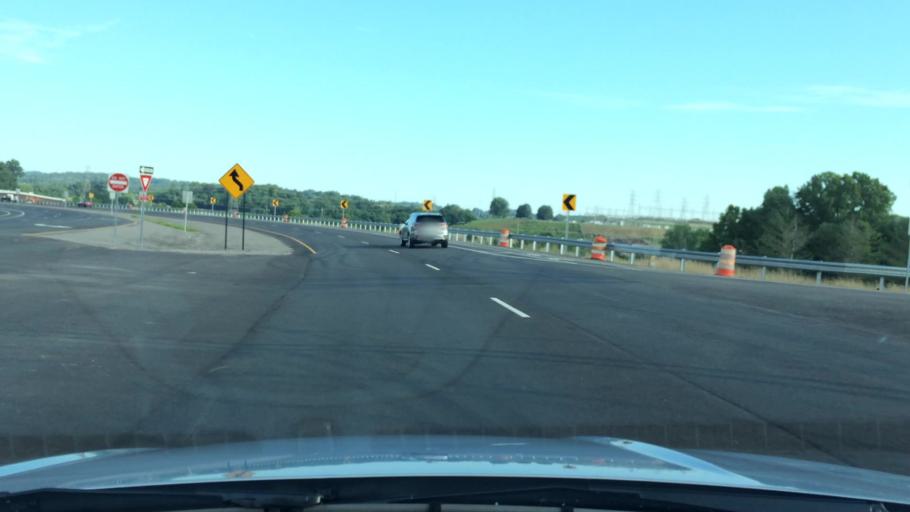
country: US
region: Tennessee
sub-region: Loudon County
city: Lenoir City
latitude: 35.7847
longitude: -84.2429
